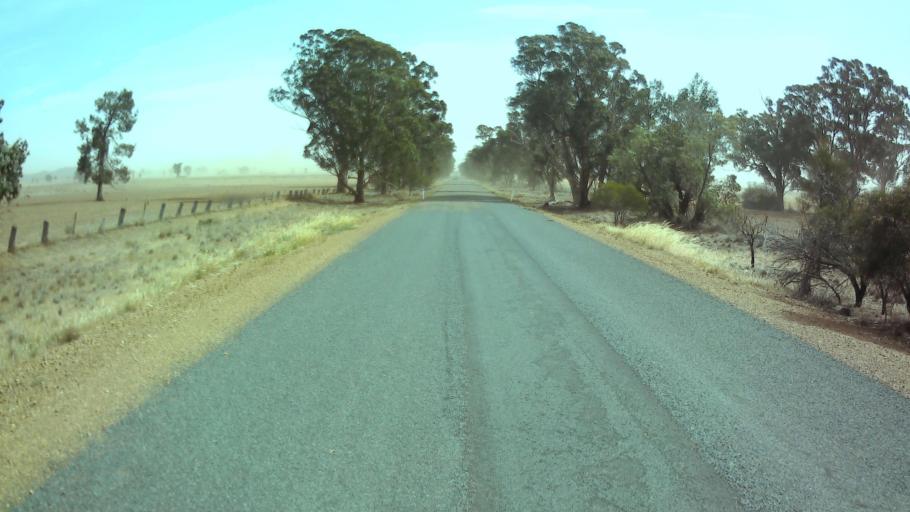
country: AU
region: New South Wales
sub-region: Weddin
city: Grenfell
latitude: -33.7613
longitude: 147.9887
